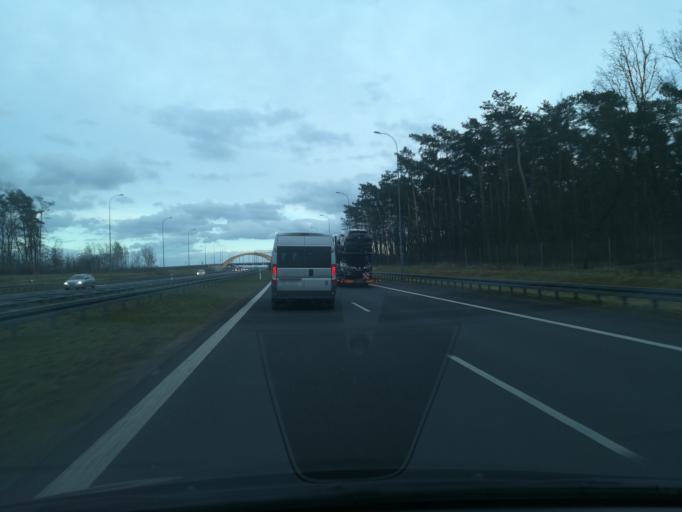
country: PL
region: Lodz Voivodeship
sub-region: Powiat kutnowski
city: Strzelce
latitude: 52.2933
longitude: 19.3840
